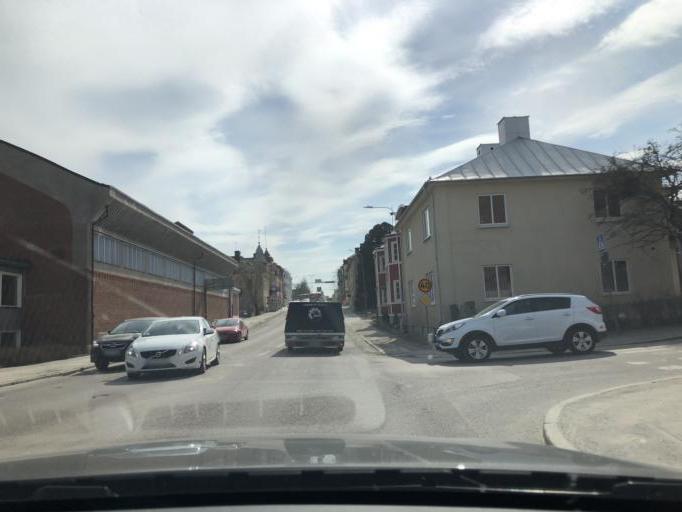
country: SE
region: Gaevleborg
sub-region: Hudiksvalls Kommun
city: Hudiksvall
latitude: 61.7285
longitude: 17.1011
